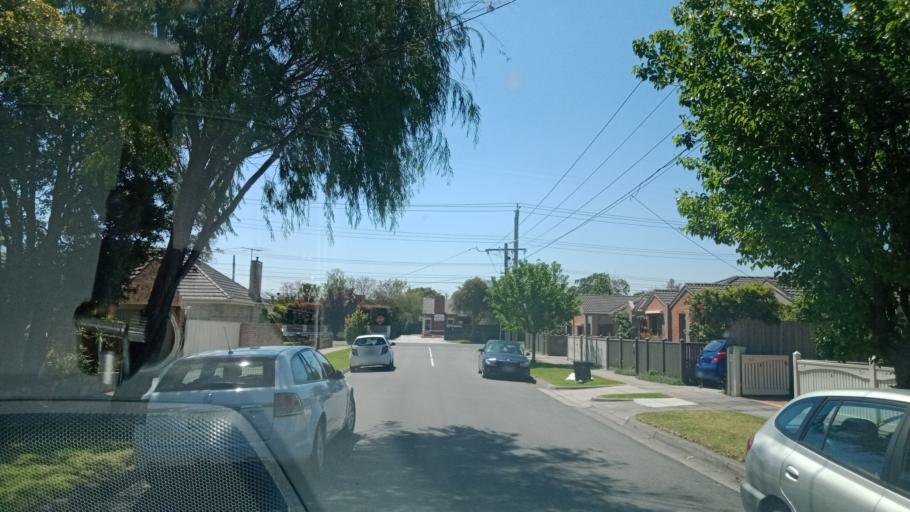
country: AU
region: Victoria
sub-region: Monash
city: Oakleigh South
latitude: -37.9240
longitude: 145.0772
